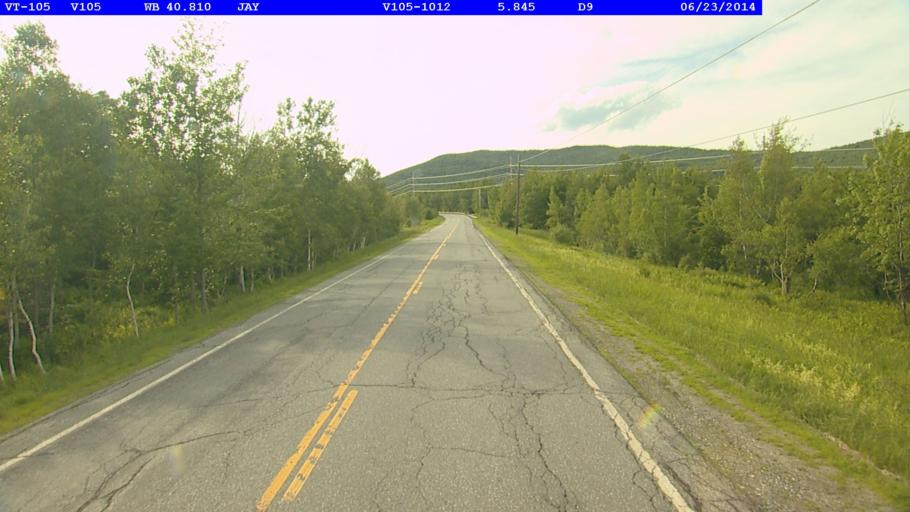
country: CA
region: Quebec
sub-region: Monteregie
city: Sutton
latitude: 44.9746
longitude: -72.4701
